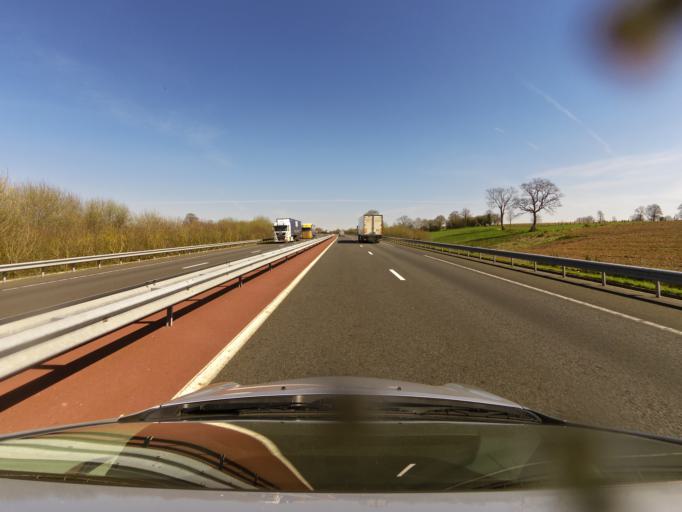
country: FR
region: Lower Normandy
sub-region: Departement de la Manche
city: Villedieu-les-Poeles
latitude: 48.7812
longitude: -1.2689
